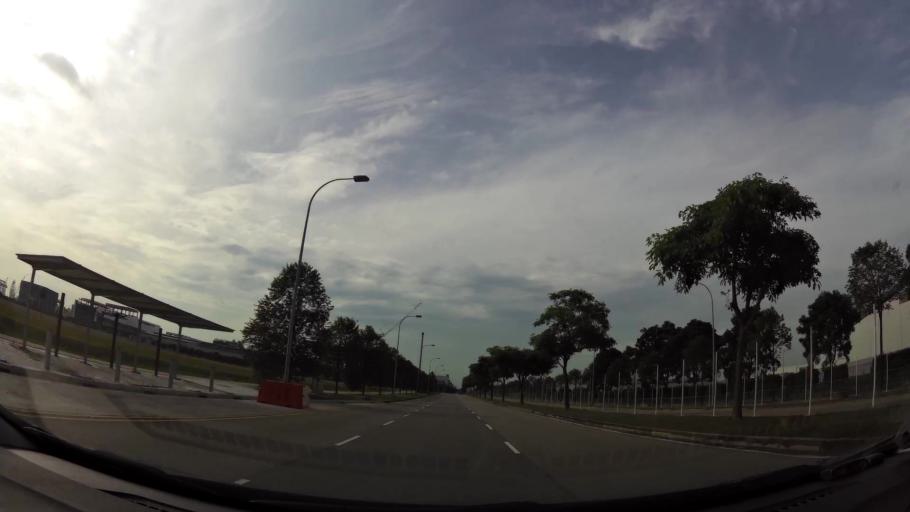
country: SG
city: Singapore
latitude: 1.2829
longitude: 103.6307
